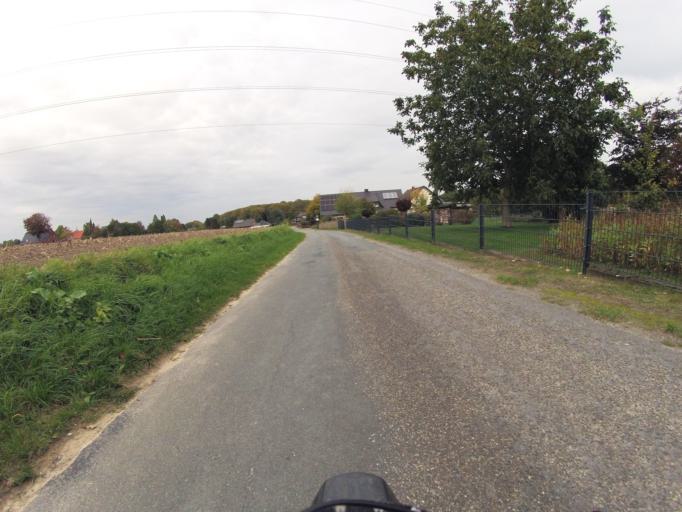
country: DE
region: North Rhine-Westphalia
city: Ibbenburen
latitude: 52.2949
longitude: 7.7445
